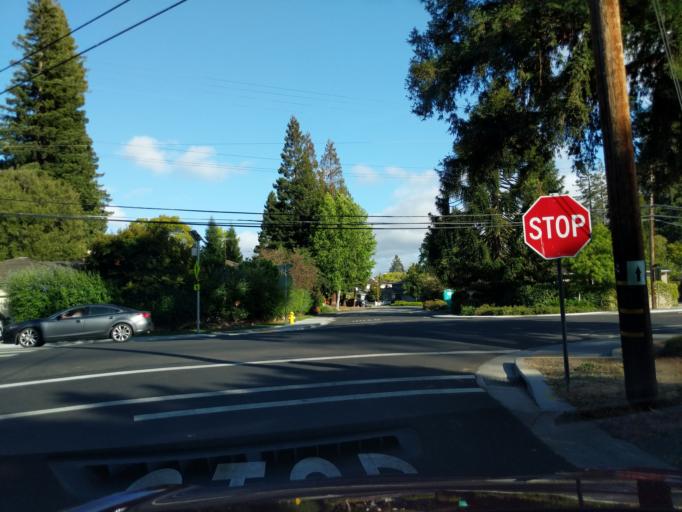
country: US
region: California
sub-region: San Mateo County
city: Menlo Park
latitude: 37.4452
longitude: -122.1902
